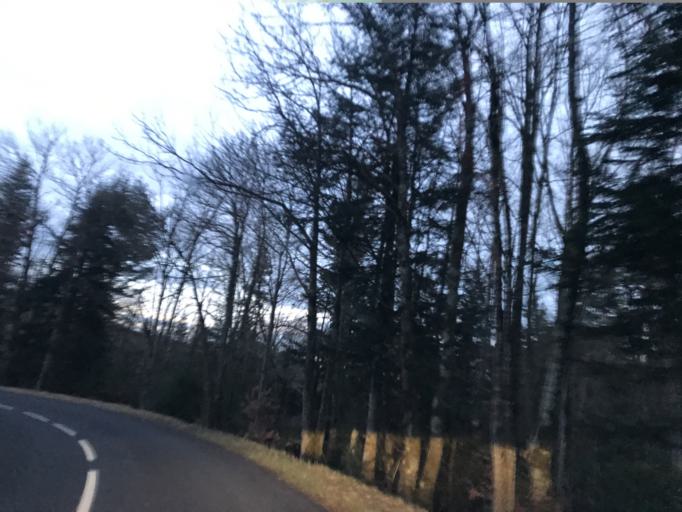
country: FR
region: Auvergne
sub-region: Departement du Puy-de-Dome
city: Saint-Remy-sur-Durolle
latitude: 45.8766
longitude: 3.5713
